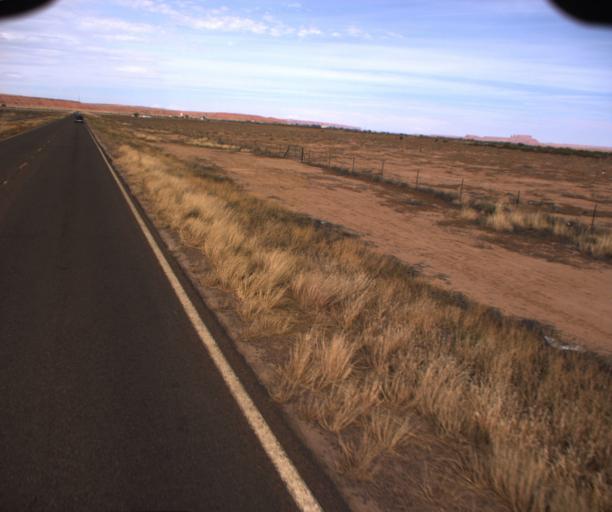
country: US
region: Arizona
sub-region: Apache County
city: Many Farms
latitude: 36.3195
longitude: -109.6156
